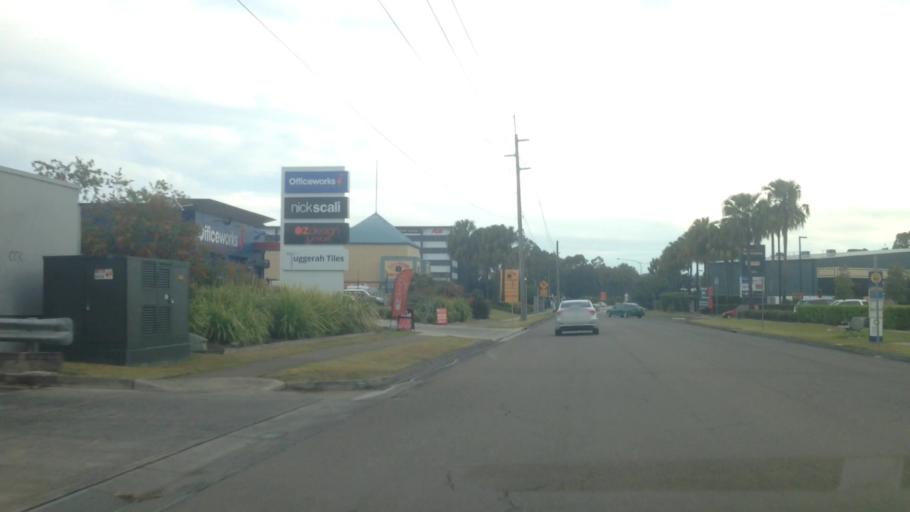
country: AU
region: New South Wales
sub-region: Wyong Shire
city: Chittaway Bay
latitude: -33.3104
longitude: 151.4226
